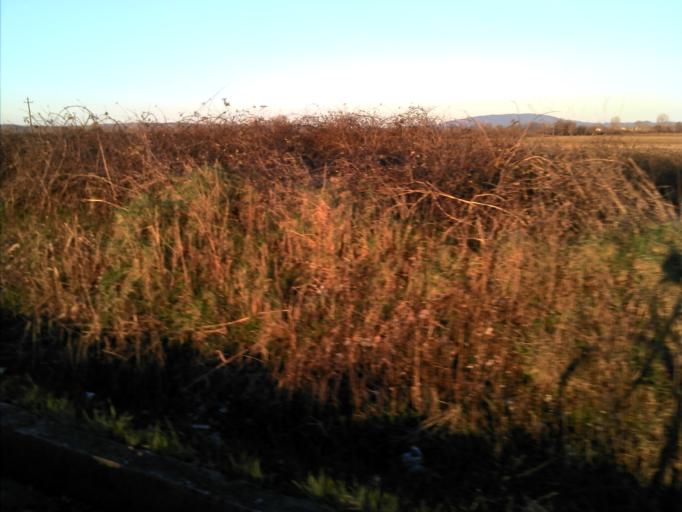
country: AL
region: Shkoder
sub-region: Rrethi i Shkodres
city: Berdica e Madhe
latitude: 41.9920
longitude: 19.4789
